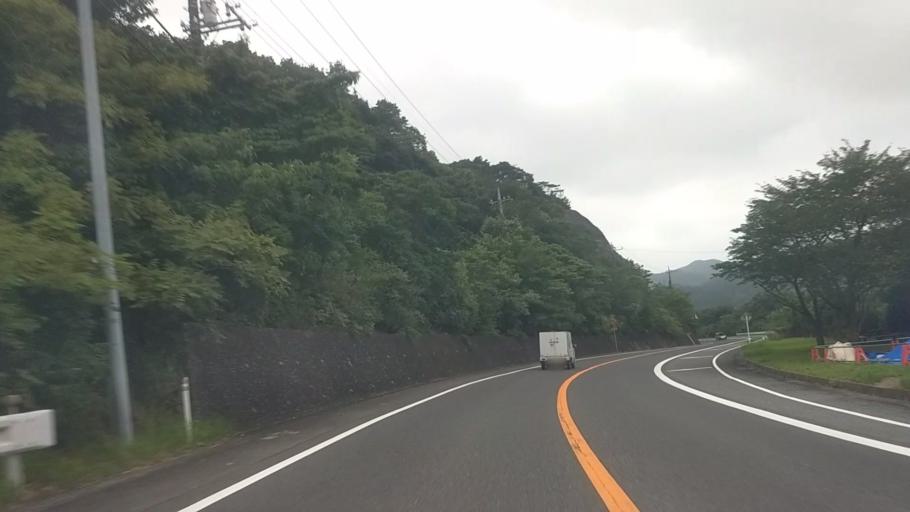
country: JP
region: Chiba
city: Kawaguchi
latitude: 35.1645
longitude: 140.0623
